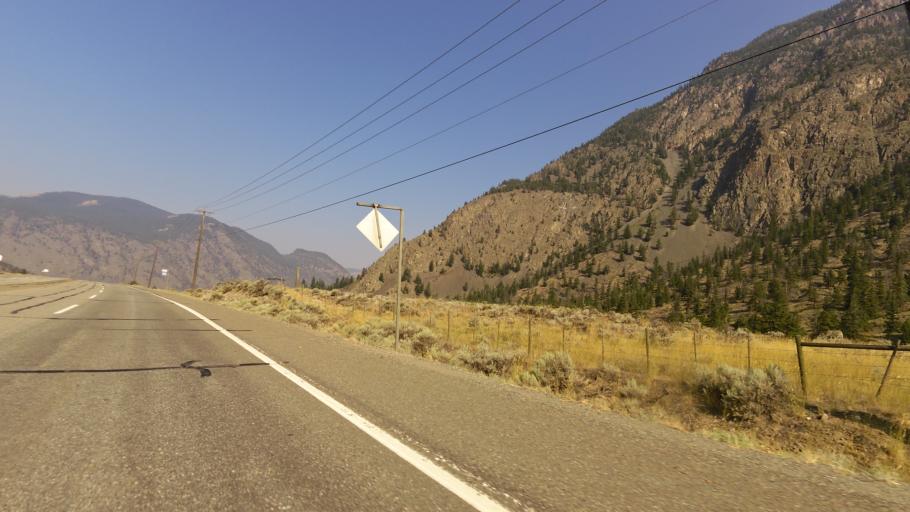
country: CA
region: British Columbia
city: Oliver
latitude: 49.2207
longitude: -119.9416
